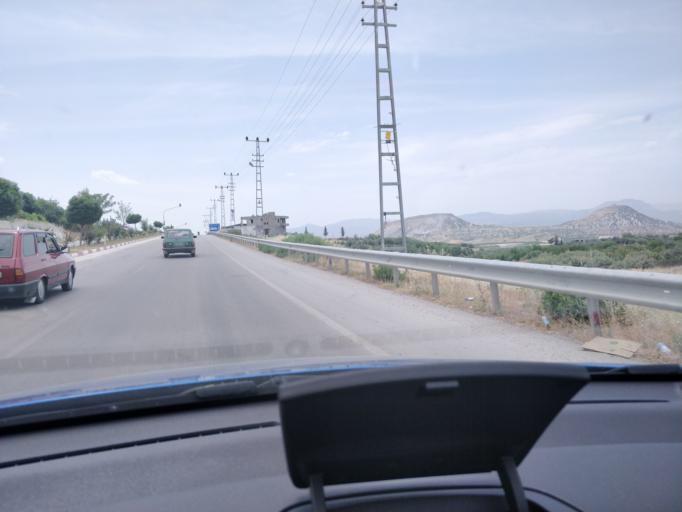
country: TR
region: Mersin
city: Mut
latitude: 36.6115
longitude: 33.4397
